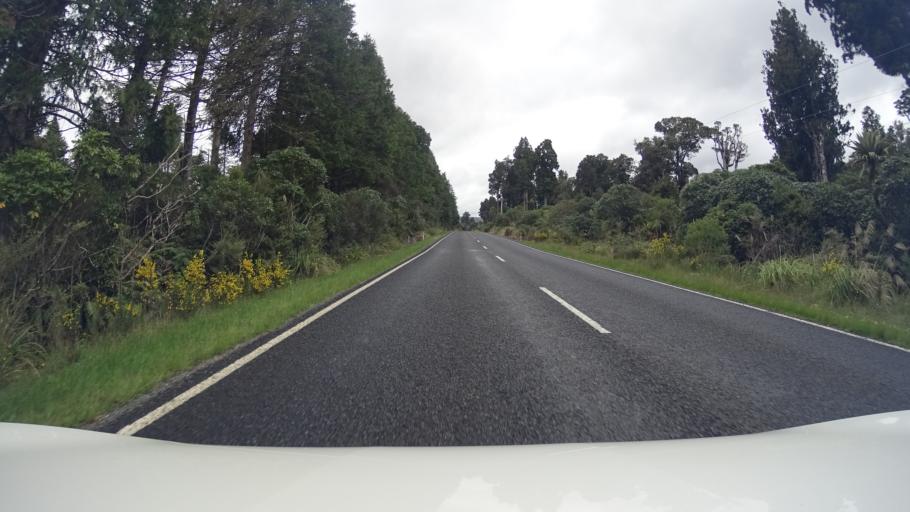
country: NZ
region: Manawatu-Wanganui
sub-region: Ruapehu District
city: Waiouru
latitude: -39.2406
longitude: 175.3917
